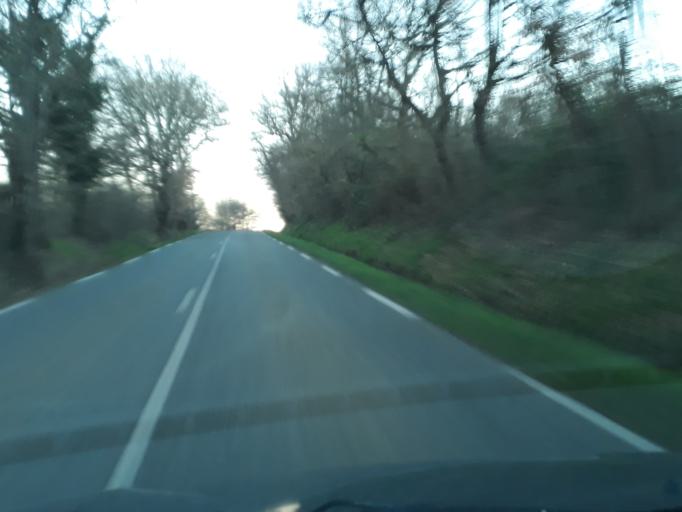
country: FR
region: Midi-Pyrenees
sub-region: Departement du Gers
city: Pujaudran
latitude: 43.5566
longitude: 1.1359
